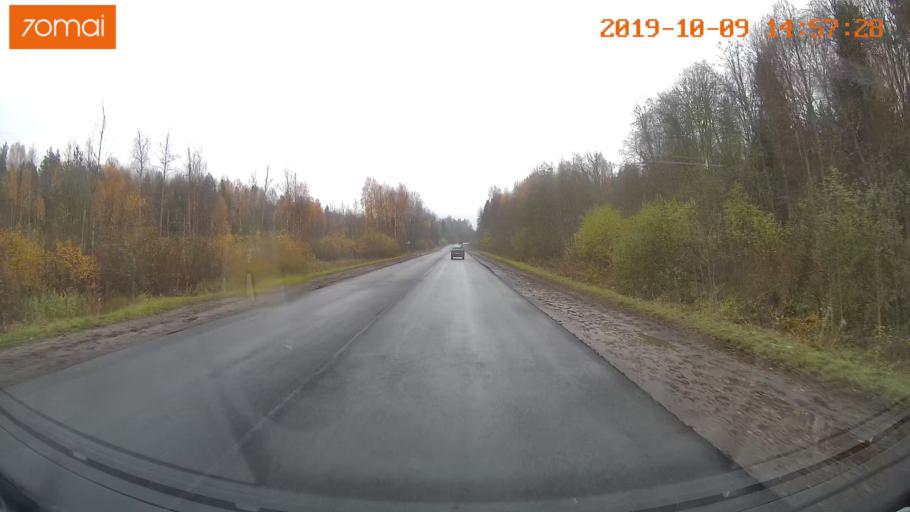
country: RU
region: Kostroma
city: Chistyye Bory
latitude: 58.3373
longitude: 41.6508
